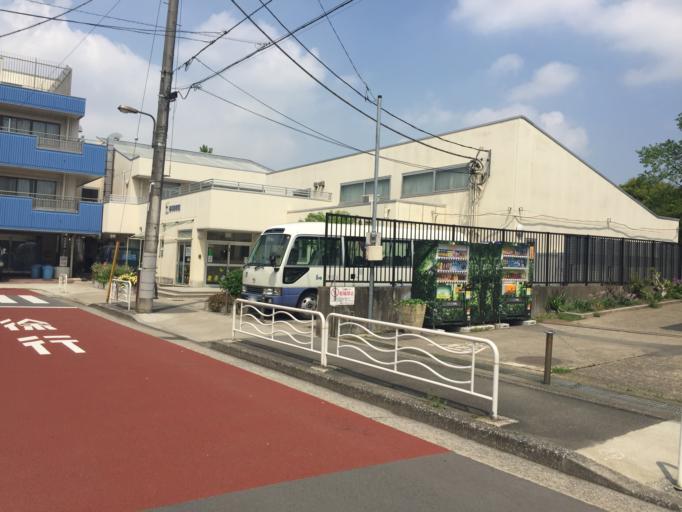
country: JP
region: Tokyo
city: Urayasu
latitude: 35.6903
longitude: 139.8163
